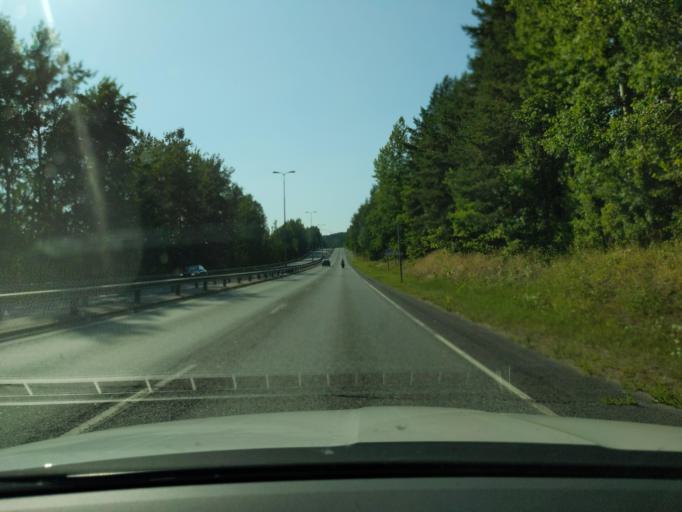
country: FI
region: Paijanne Tavastia
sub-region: Lahti
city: Lahti
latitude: 60.9736
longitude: 25.6969
